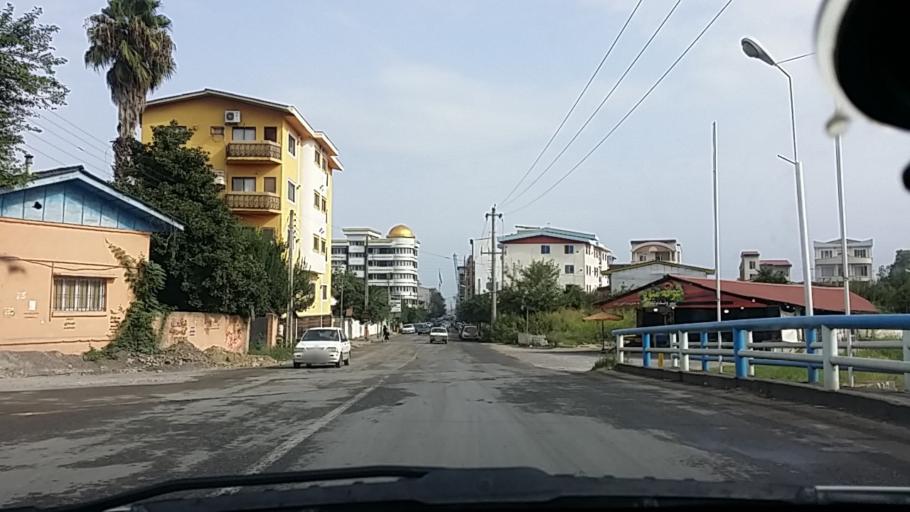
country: IR
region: Mazandaran
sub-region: Nowshahr
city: Nowshahr
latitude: 36.6470
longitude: 51.5085
